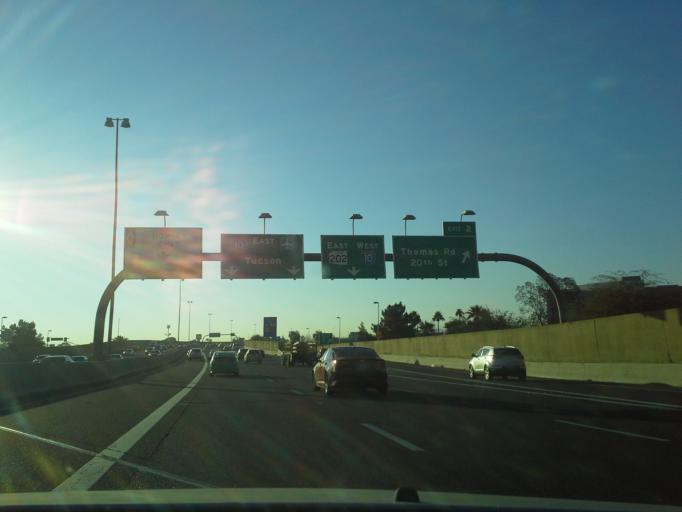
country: US
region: Arizona
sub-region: Maricopa County
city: Phoenix
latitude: 33.4852
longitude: -112.0410
